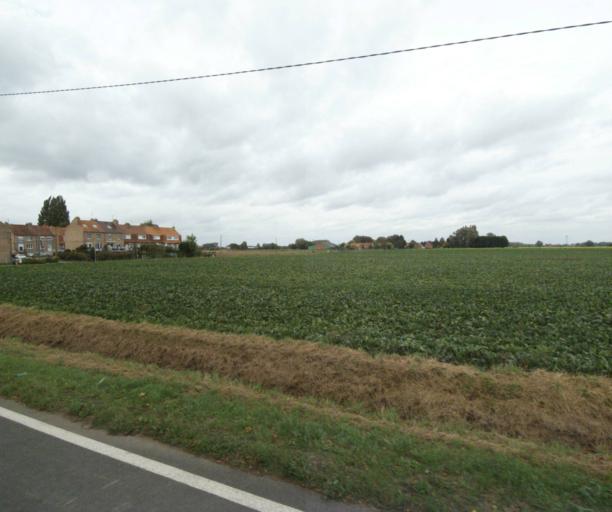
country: FR
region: Nord-Pas-de-Calais
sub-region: Departement du Nord
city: Houplines
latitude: 50.6636
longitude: 2.9206
